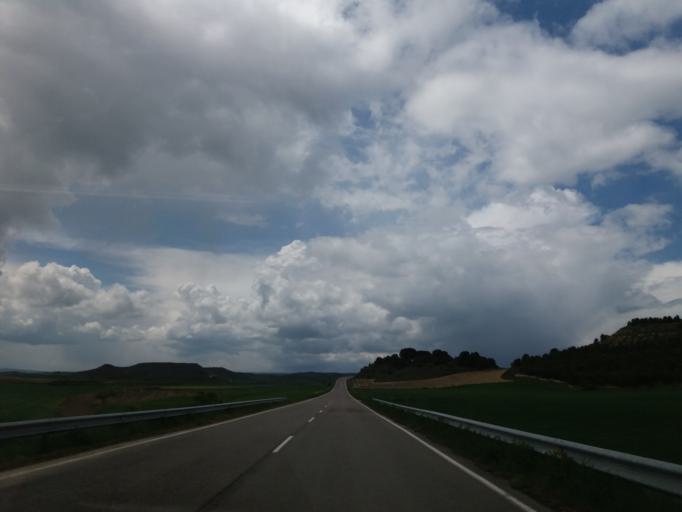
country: ES
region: La Rioja
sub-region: Provincia de La Rioja
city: Sajazarra
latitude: 42.5657
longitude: -2.9692
